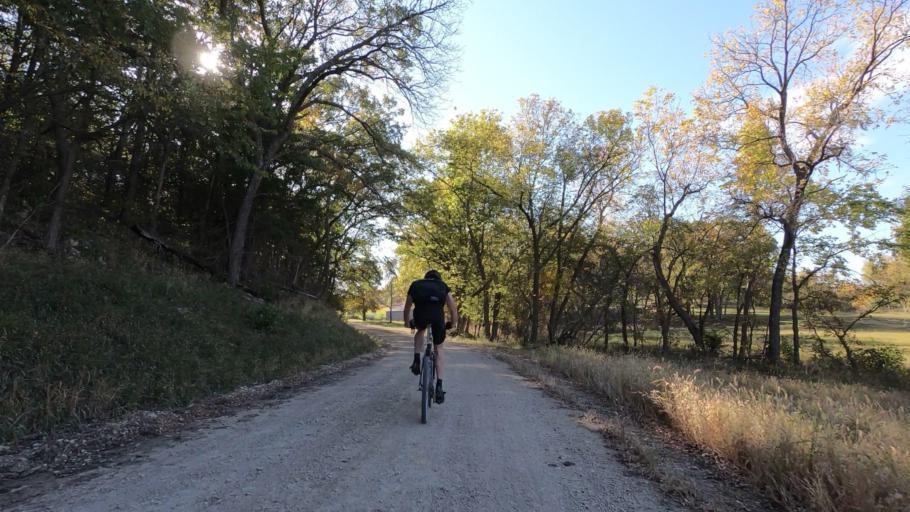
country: US
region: Kansas
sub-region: Pottawatomie County
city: Westmoreland
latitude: 39.4837
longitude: -96.5981
